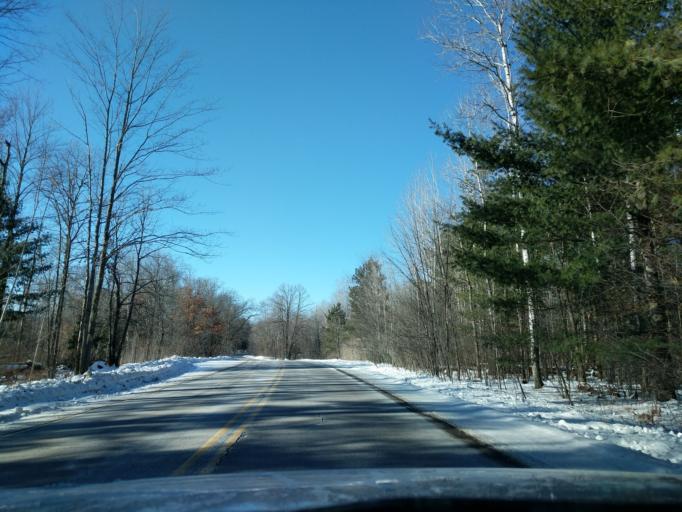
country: US
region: Wisconsin
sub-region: Menominee County
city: Keshena
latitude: 45.1158
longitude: -88.6510
